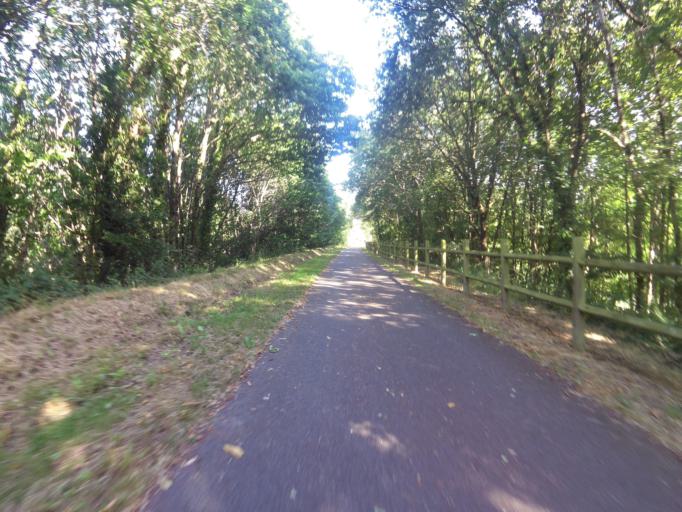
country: FR
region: Brittany
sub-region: Departement du Morbihan
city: Malestroit
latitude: 47.8133
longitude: -2.4079
